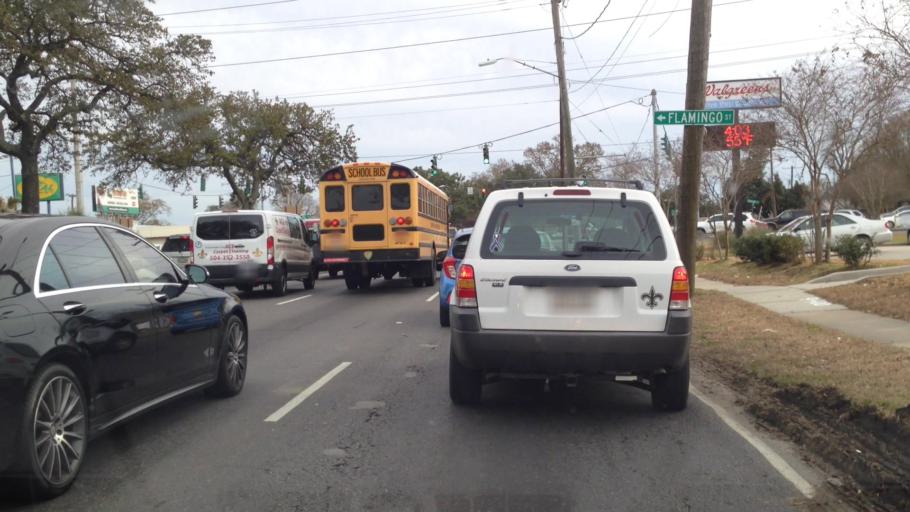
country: US
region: Louisiana
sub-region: Jefferson Parish
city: Metairie Terrace
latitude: 29.9762
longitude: -90.1784
